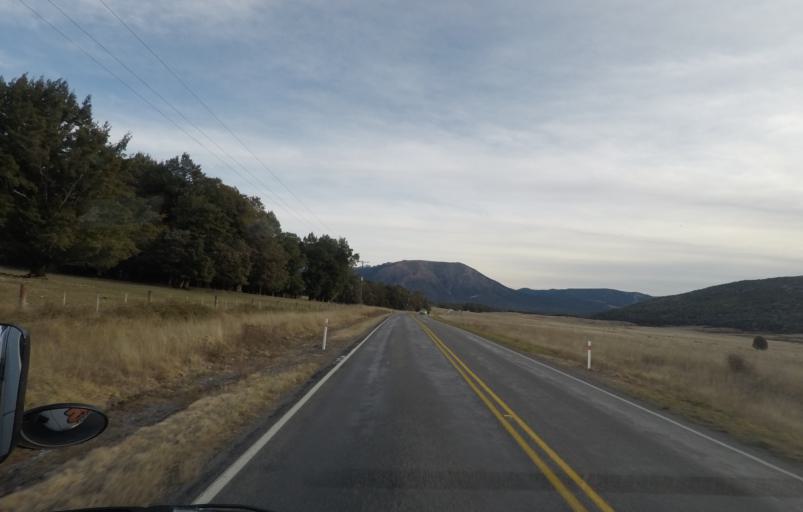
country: NZ
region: Tasman
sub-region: Tasman District
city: Wakefield
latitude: -41.7933
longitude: 172.8784
